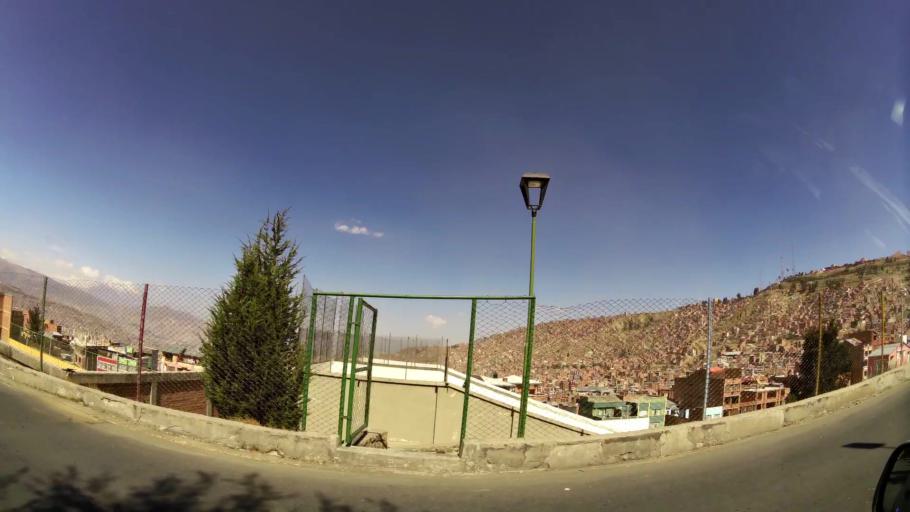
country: BO
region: La Paz
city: La Paz
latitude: -16.4875
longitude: -68.1592
